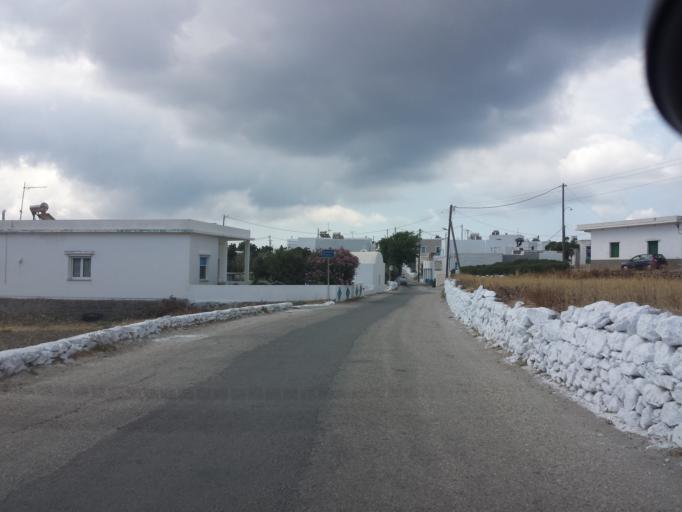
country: GR
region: South Aegean
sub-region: Nomos Kykladon
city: Milos
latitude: 36.7418
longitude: 24.4247
